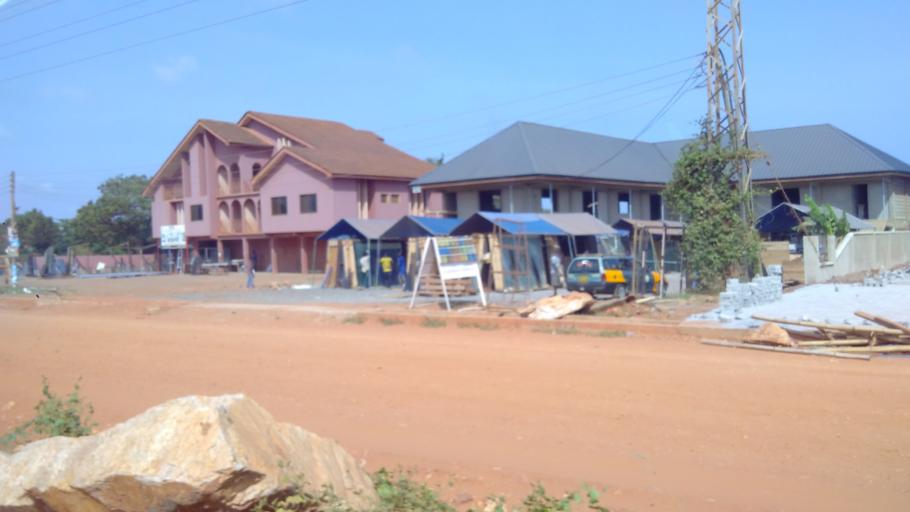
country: GH
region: Greater Accra
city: Nungua
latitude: 5.6308
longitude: -0.0660
